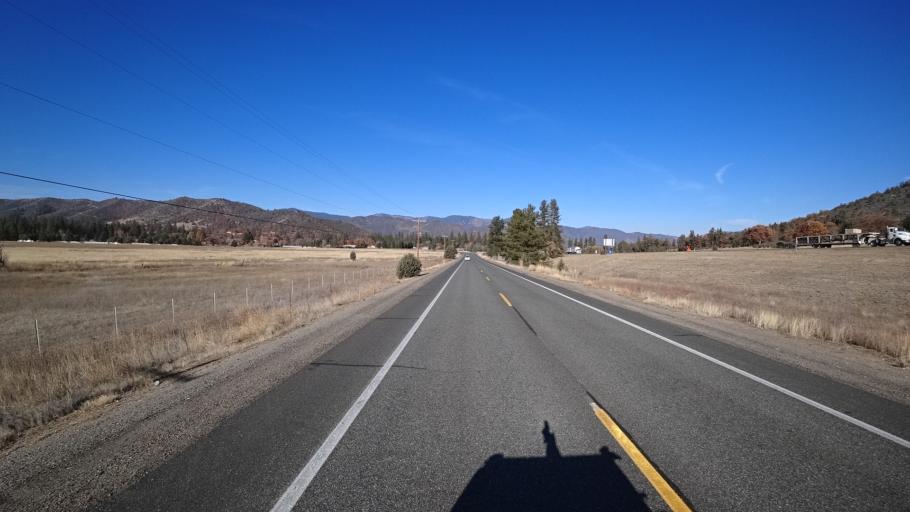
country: US
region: California
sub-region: Siskiyou County
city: Yreka
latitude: 41.6789
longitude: -122.6290
